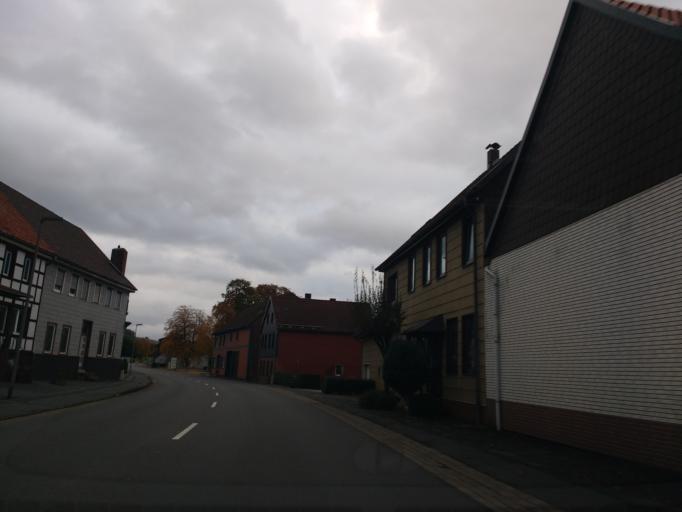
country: DE
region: Lower Saxony
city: Bad Lauterberg im Harz
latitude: 51.5904
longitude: 10.4866
